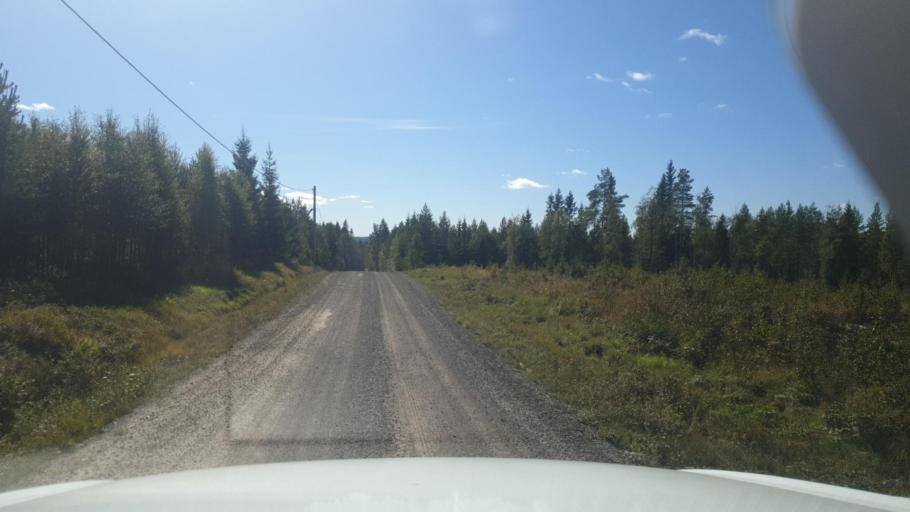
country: SE
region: Vaermland
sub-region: Eda Kommun
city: Charlottenberg
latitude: 60.1573
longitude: 12.6009
